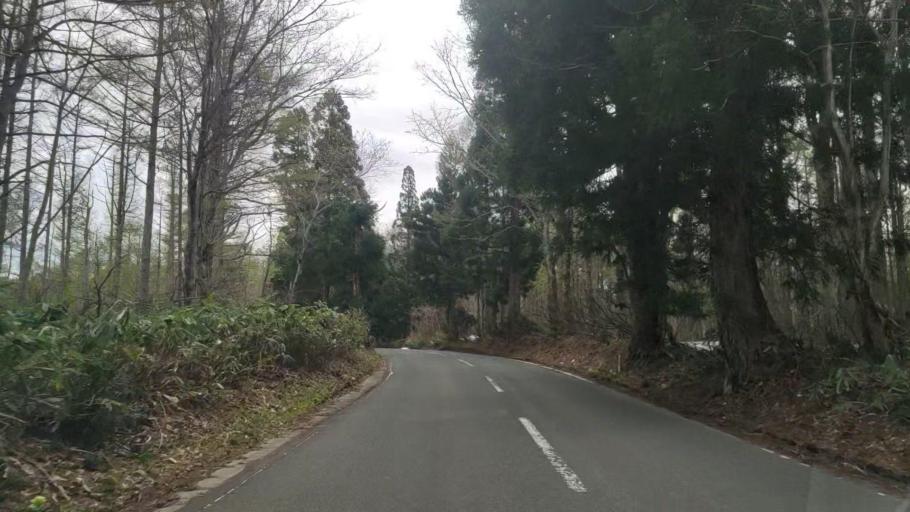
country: JP
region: Aomori
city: Aomori Shi
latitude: 40.7203
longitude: 140.8590
